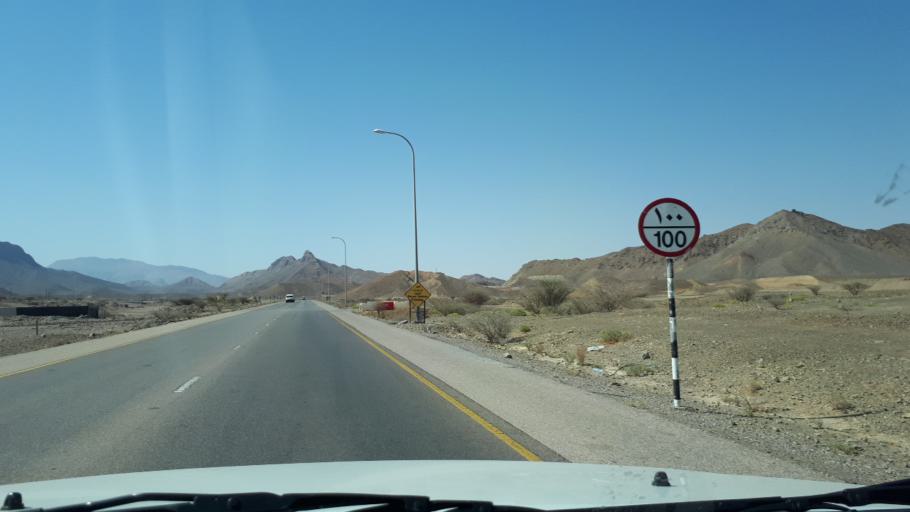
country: OM
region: Ash Sharqiyah
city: Sur
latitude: 22.3559
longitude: 59.3126
